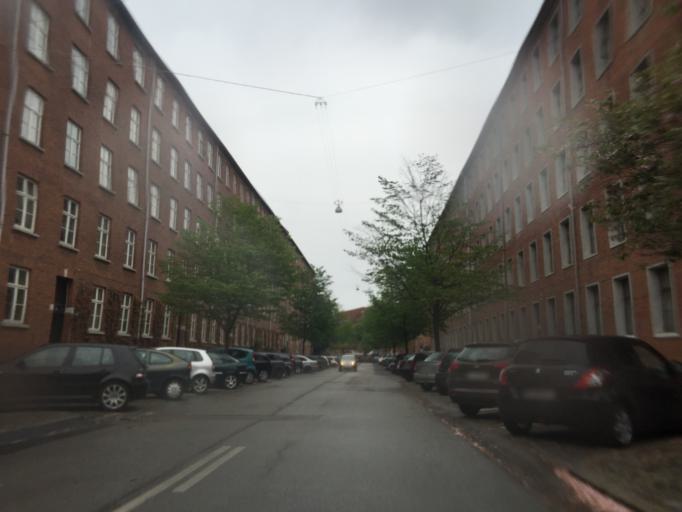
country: DK
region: Capital Region
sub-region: Kobenhavn
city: Vanlose
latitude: 55.6803
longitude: 12.5059
